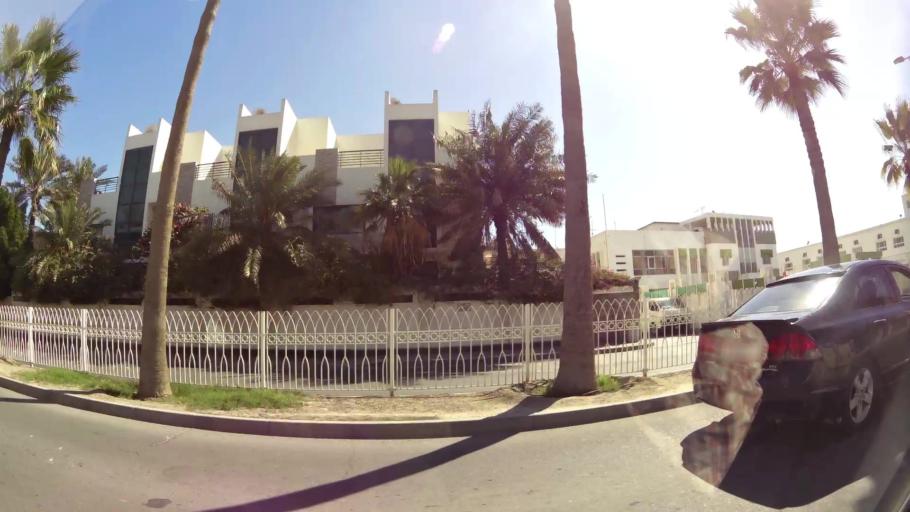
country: BH
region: Muharraq
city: Al Muharraq
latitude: 26.2595
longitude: 50.6077
